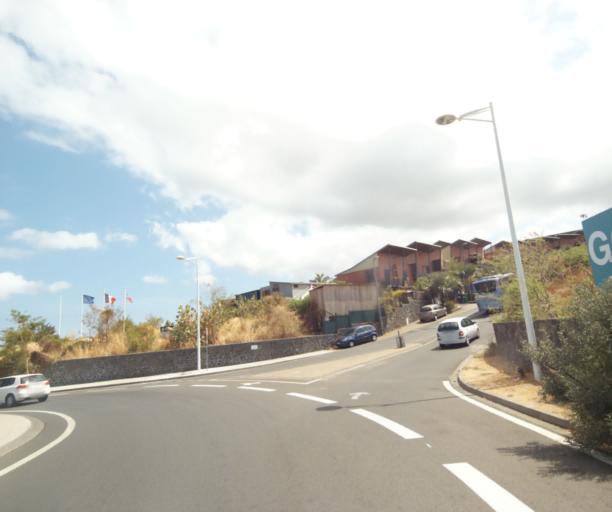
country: RE
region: Reunion
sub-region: Reunion
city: Trois-Bassins
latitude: -21.0879
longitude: 55.2379
